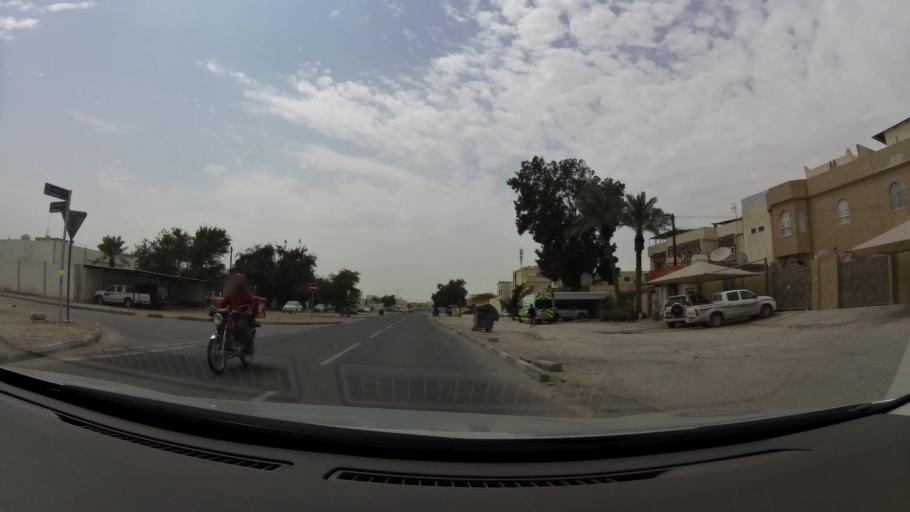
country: QA
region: Baladiyat ar Rayyan
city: Ar Rayyan
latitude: 25.3323
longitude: 51.4725
